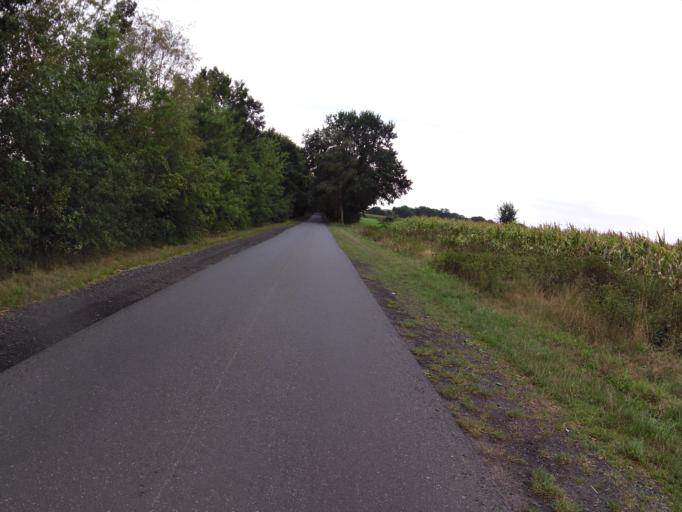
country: DE
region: Lower Saxony
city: Helvesiek
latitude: 53.2026
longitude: 9.4618
